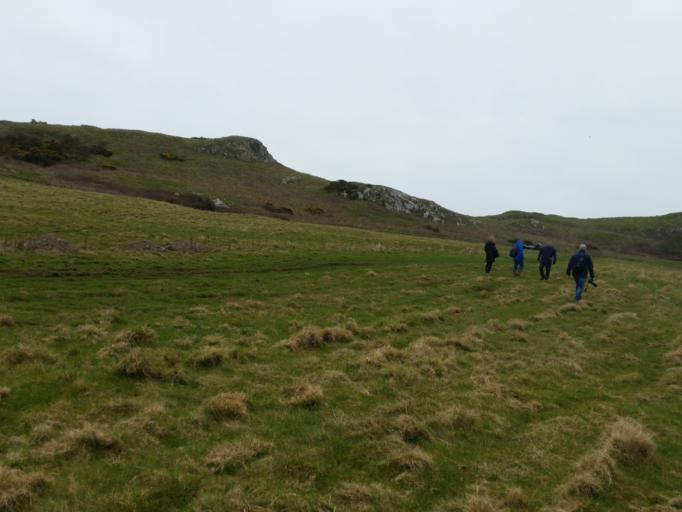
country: IE
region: Leinster
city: Portraine
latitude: 53.4908
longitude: -6.0214
